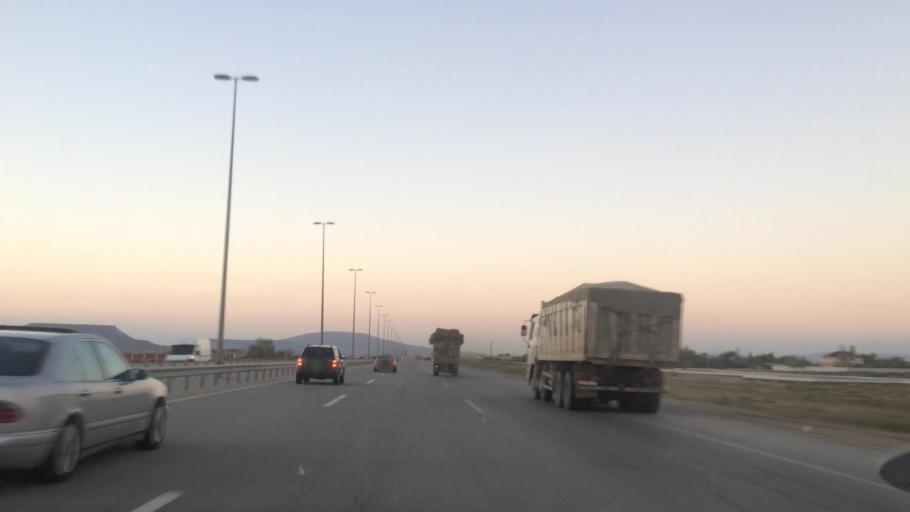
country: AZ
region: Baki
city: Qobustan
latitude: 40.0185
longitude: 49.4255
